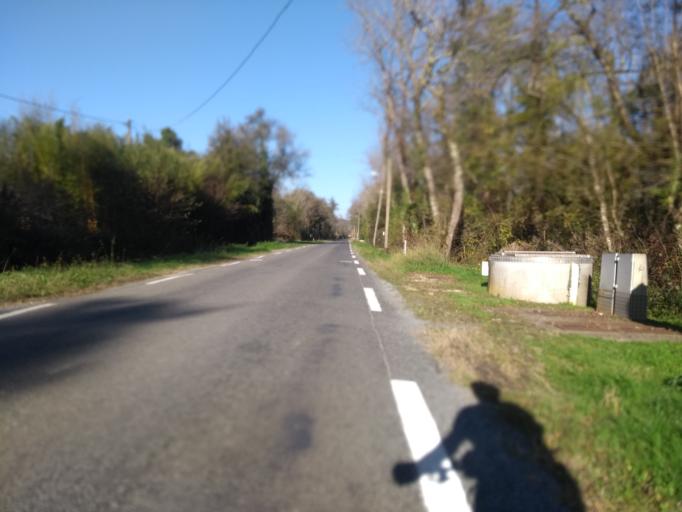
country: FR
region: Aquitaine
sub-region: Departement de la Gironde
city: Ayguemorte-les-Graves
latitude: 44.7155
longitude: -0.4700
